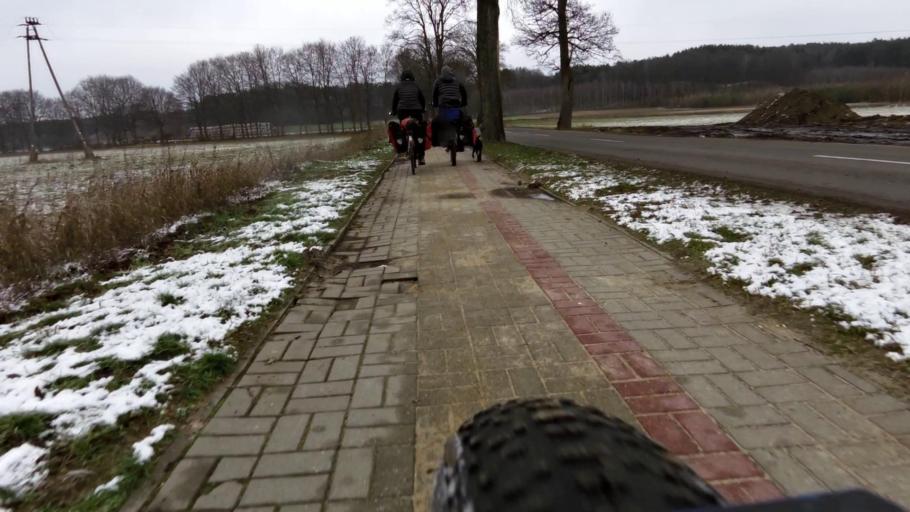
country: PL
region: West Pomeranian Voivodeship
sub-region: Powiat walecki
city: Miroslawiec
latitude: 53.3523
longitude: 16.0860
